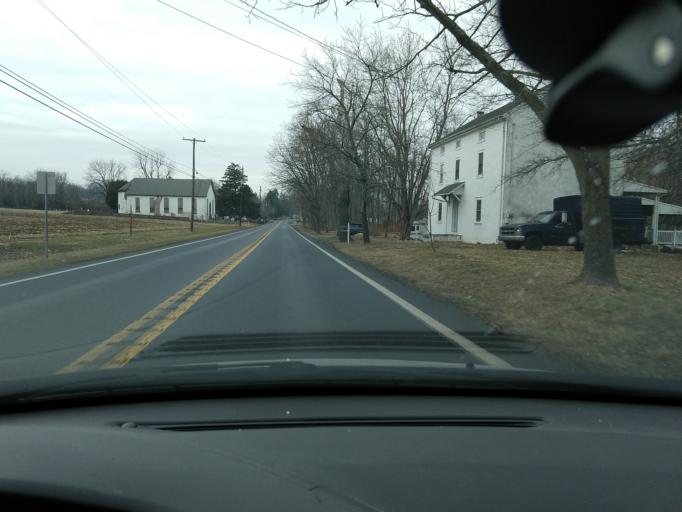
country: US
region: Pennsylvania
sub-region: Berks County
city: Amity Gardens
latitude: 40.2577
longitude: -75.7465
